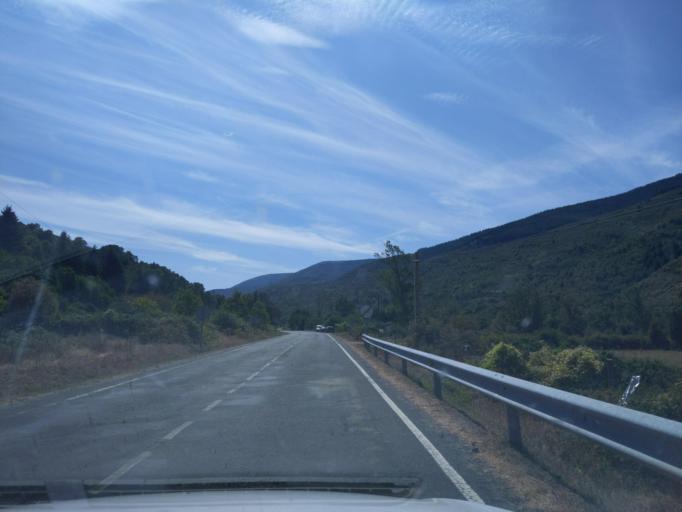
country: ES
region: La Rioja
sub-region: Provincia de La Rioja
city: Ezcaray
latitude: 42.3043
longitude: -3.0226
